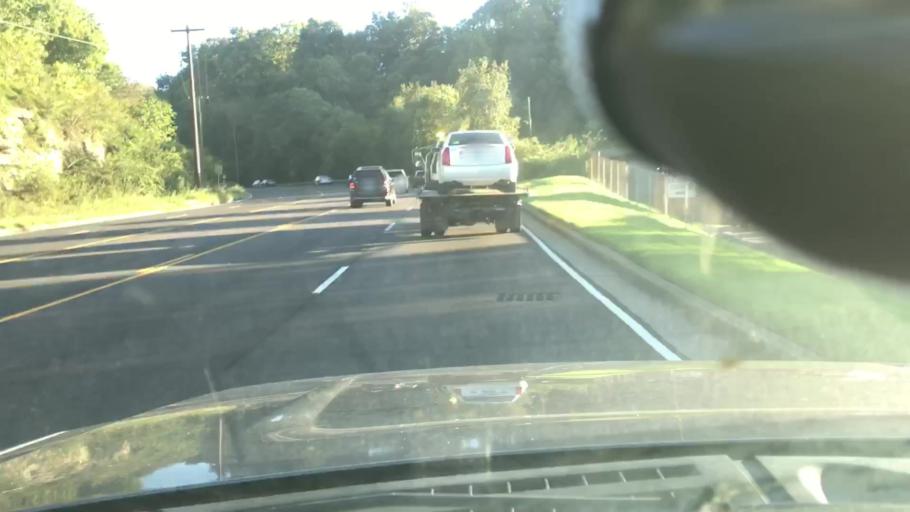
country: US
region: Tennessee
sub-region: Davidson County
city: Belle Meade
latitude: 36.0726
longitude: -86.9208
